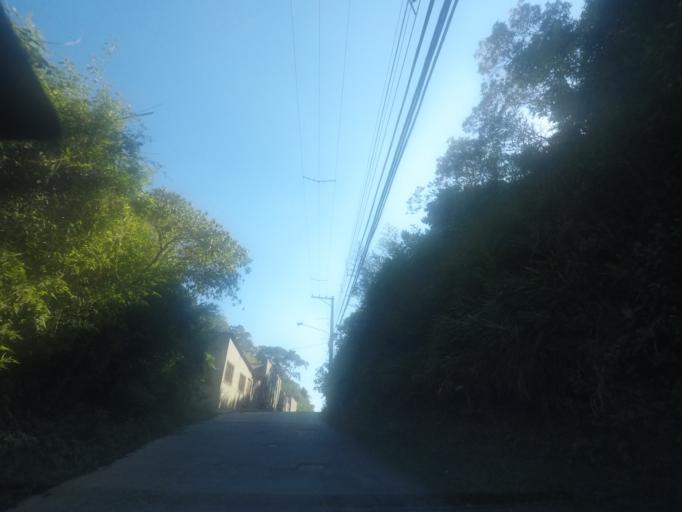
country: BR
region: Rio de Janeiro
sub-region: Petropolis
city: Petropolis
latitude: -22.5392
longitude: -43.2011
